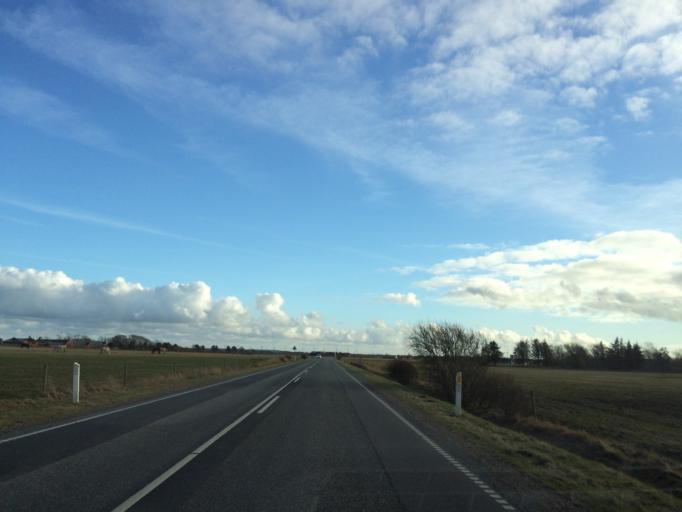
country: DK
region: Central Jutland
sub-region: Lemvig Kommune
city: Lemvig
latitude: 56.4336
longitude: 8.2988
